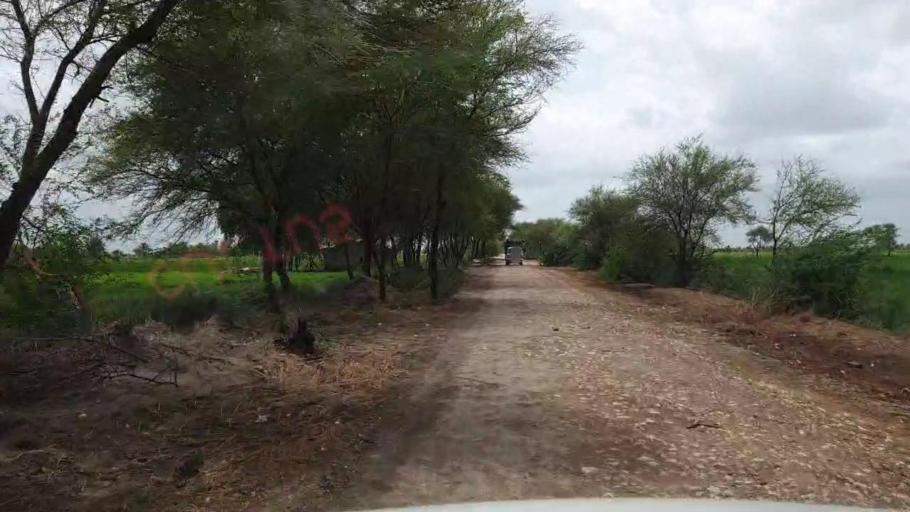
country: PK
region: Sindh
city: Kario
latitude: 24.7406
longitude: 68.5229
